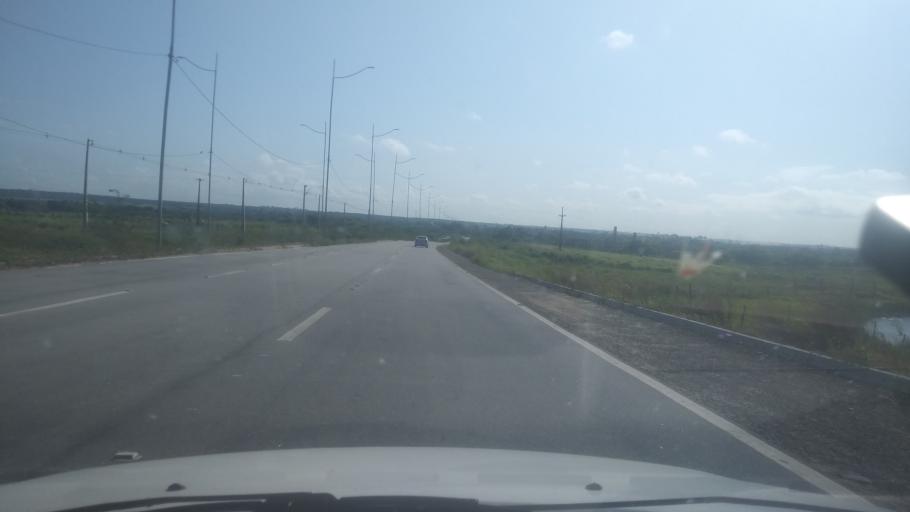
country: BR
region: Rio Grande do Norte
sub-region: Macaiba
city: Macaiba
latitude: -5.8204
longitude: -35.3661
